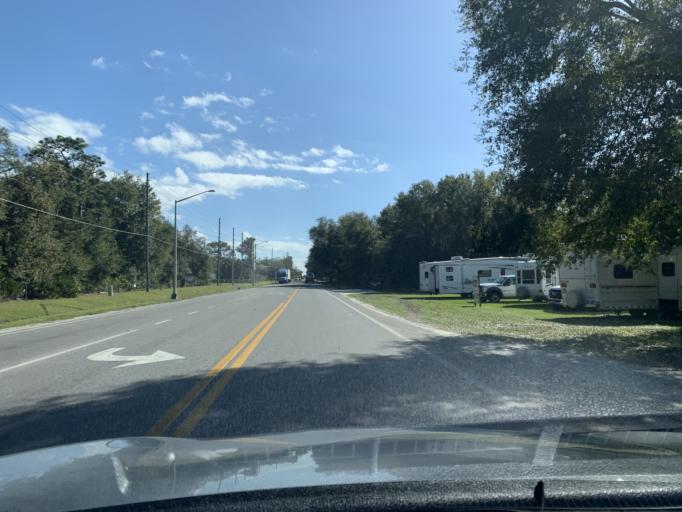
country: US
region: Florida
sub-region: Seminole County
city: Forest City
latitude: 28.6480
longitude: -81.4717
